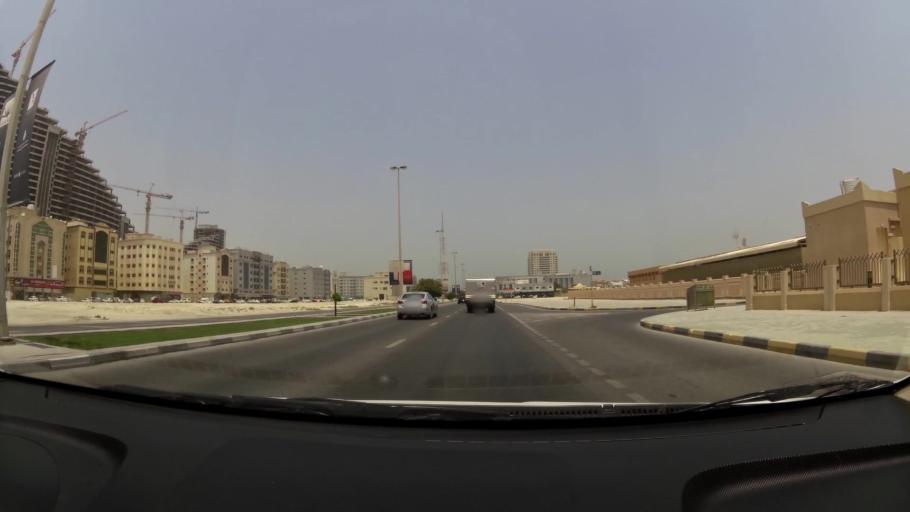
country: AE
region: Ash Shariqah
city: Sharjah
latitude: 25.3322
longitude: 55.3664
